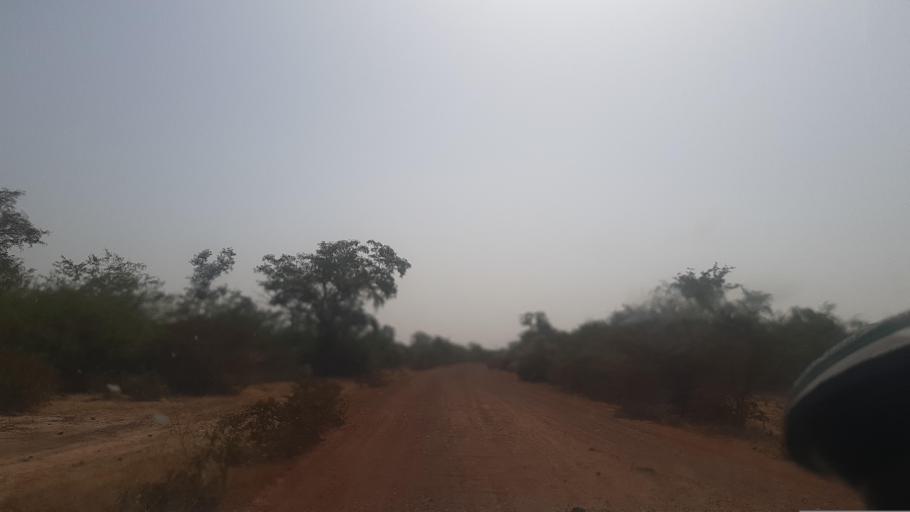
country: ML
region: Segou
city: Baroueli
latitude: 13.0648
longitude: -6.4759
